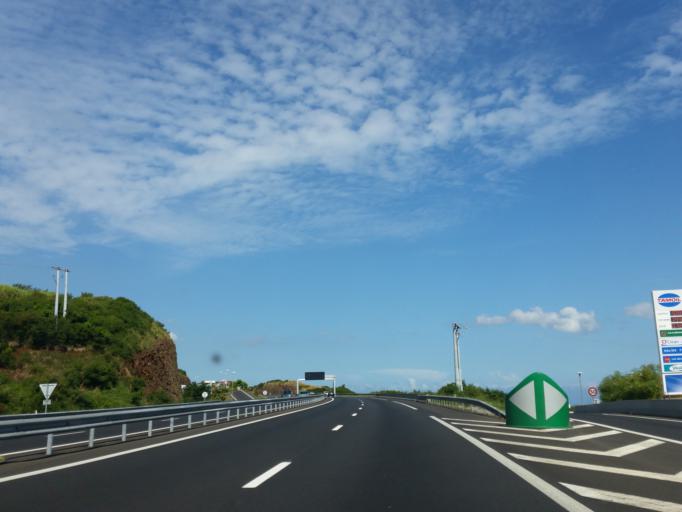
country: RE
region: Reunion
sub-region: Reunion
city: Trois-Bassins
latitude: -21.0860
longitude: 55.2560
